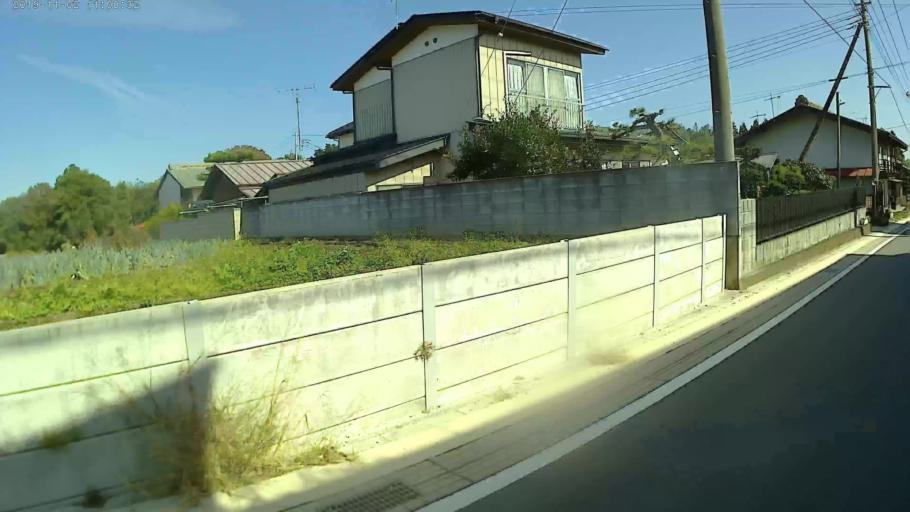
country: JP
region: Gunma
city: Annaka
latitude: 36.3065
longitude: 138.8274
